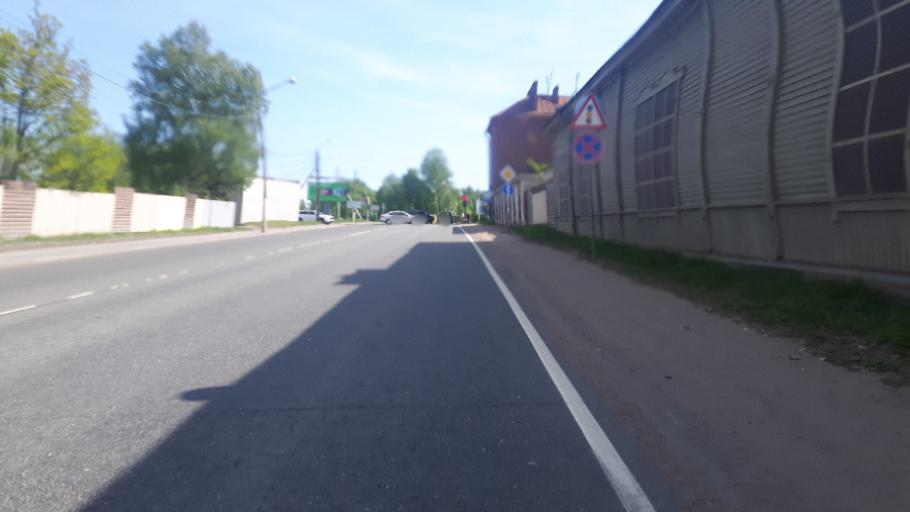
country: RU
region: Leningrad
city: Vyborg
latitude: 60.7215
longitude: 28.7174
